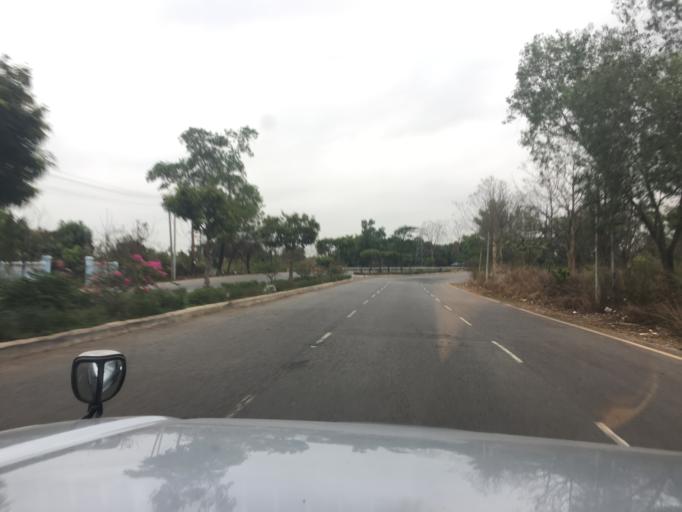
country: MM
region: Bago
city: Thanatpin
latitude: 17.2106
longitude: 96.4167
